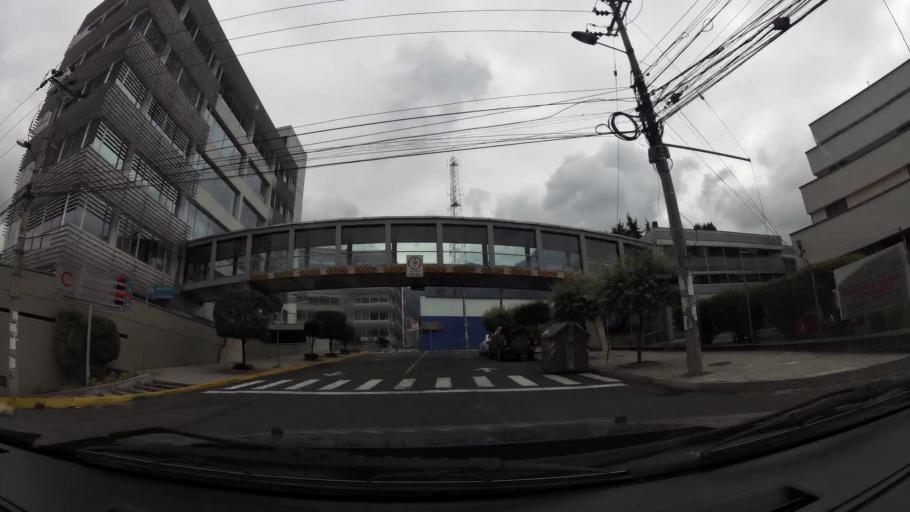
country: EC
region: Pichincha
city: Quito
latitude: -0.1854
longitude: -78.5039
